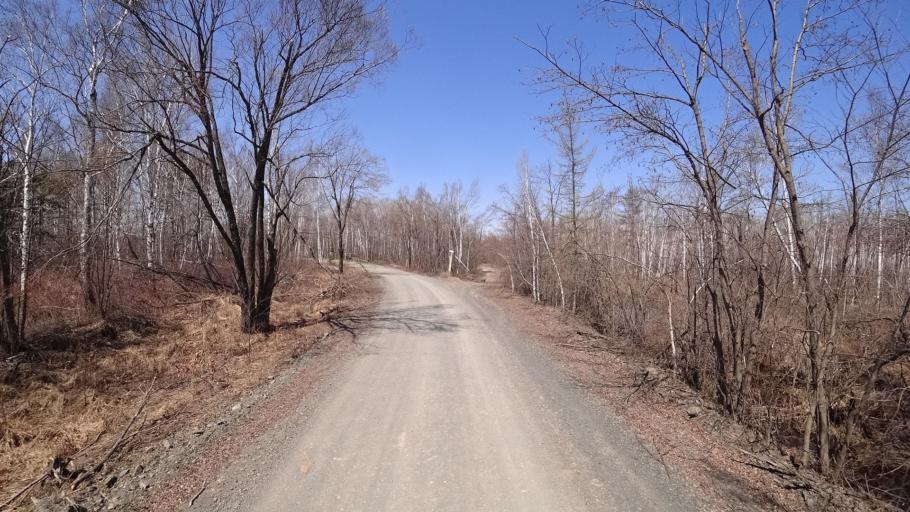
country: RU
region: Khabarovsk Krai
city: Khurba
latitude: 50.4198
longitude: 136.8327
